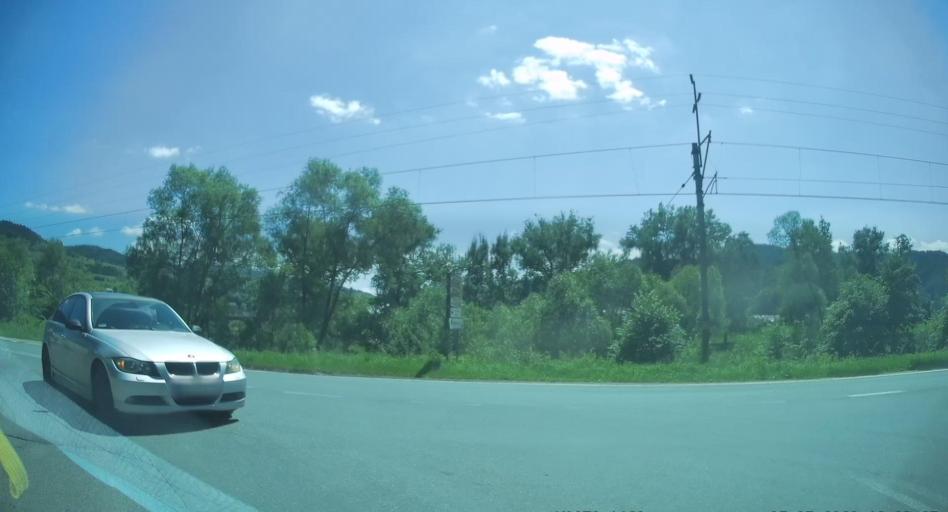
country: PL
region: Lesser Poland Voivodeship
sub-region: Powiat nowosadecki
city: Muszyna
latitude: 49.3529
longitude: 20.8892
